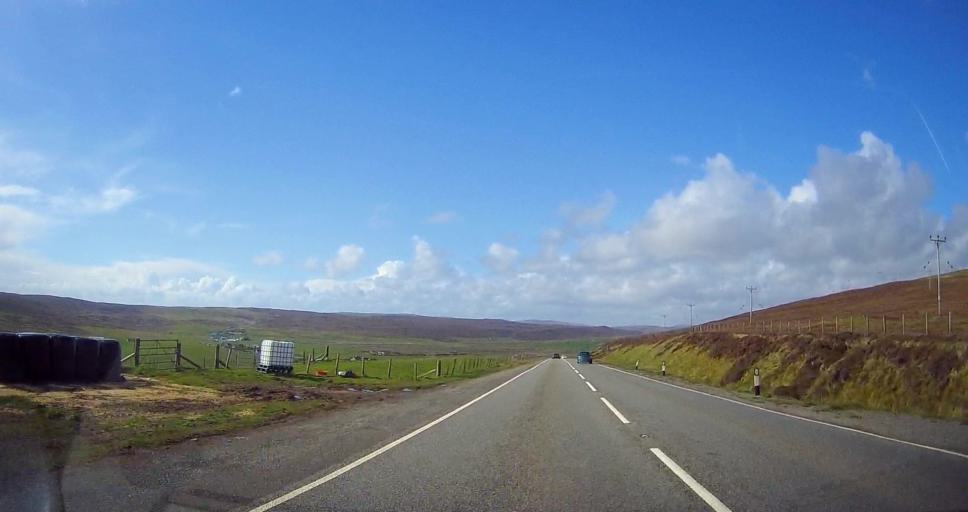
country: GB
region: Scotland
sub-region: Shetland Islands
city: Lerwick
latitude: 60.1767
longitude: -1.2228
